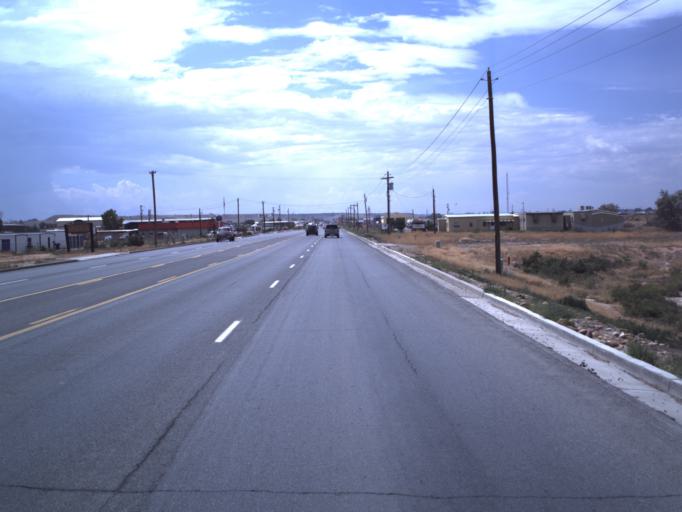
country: US
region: Utah
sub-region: Duchesne County
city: Roosevelt
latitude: 40.2822
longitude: -110.0135
